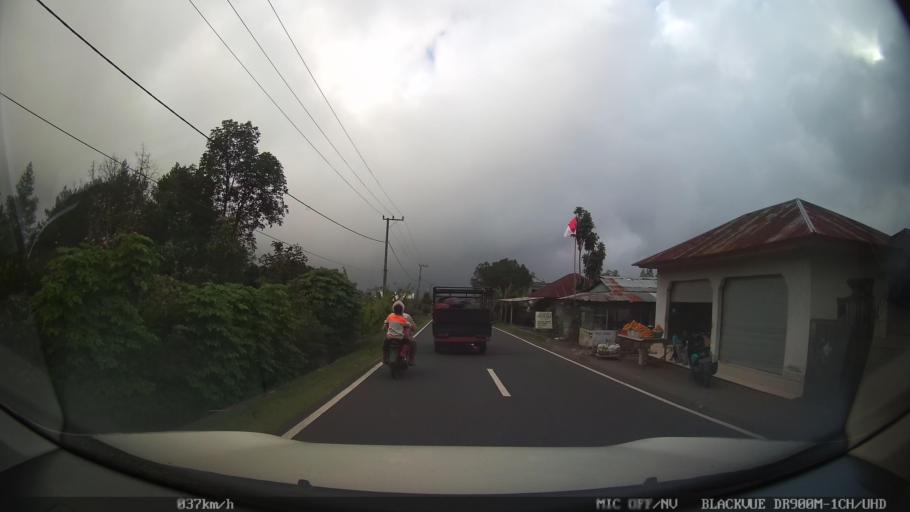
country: ID
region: Bali
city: Banjar Kedisan
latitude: -8.2721
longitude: 115.3303
